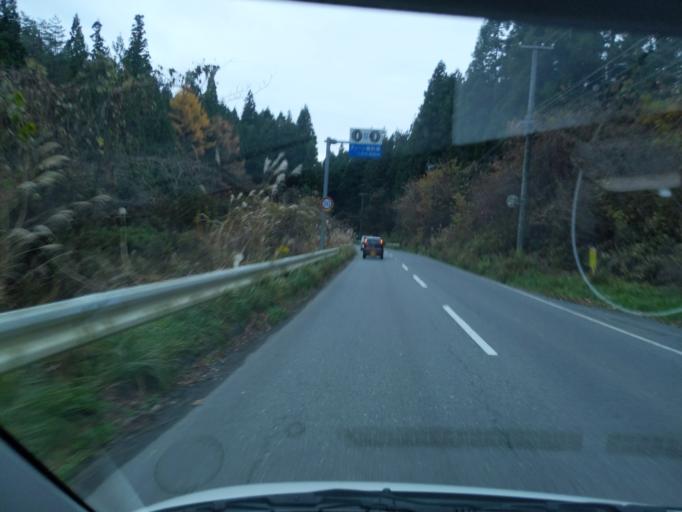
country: JP
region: Iwate
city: Mizusawa
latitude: 39.0263
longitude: 141.3334
